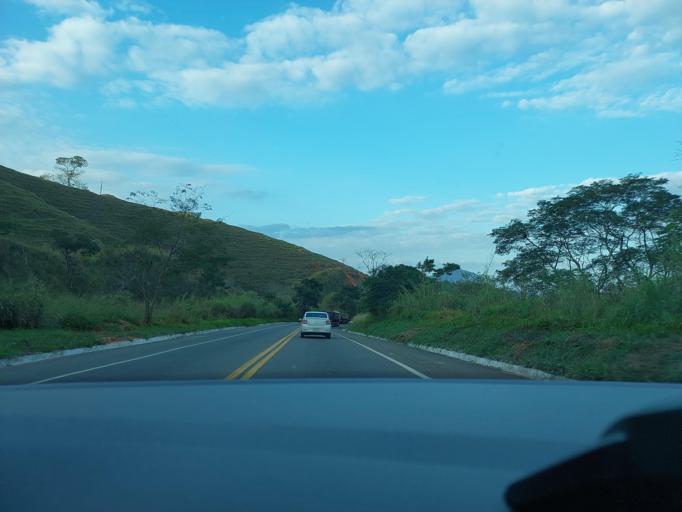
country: BR
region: Minas Gerais
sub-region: Muriae
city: Muriae
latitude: -21.1239
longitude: -42.2296
